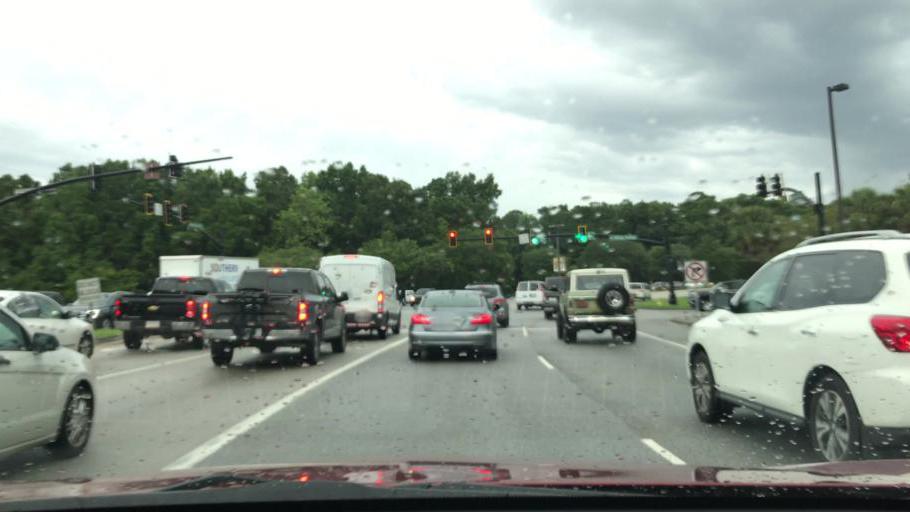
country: US
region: South Carolina
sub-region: Berkeley County
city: Hanahan
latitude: 32.8717
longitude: -80.0384
